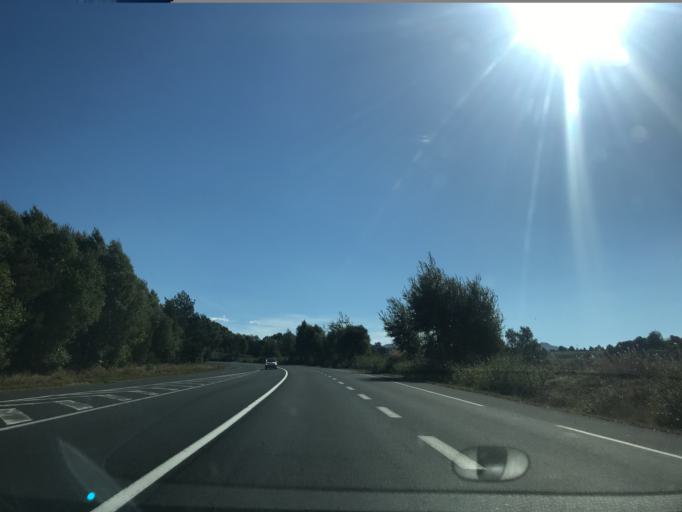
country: FR
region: Auvergne
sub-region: Departement du Puy-de-Dome
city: La Bourboule
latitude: 45.6656
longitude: 2.7293
